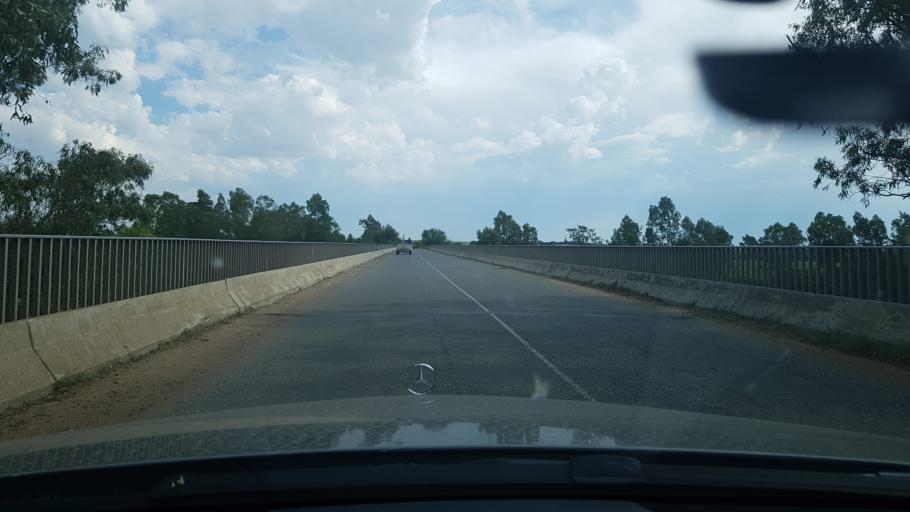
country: ZA
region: North-West
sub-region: Dr Ruth Segomotsi Mompati District Municipality
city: Bloemhof
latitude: -27.6539
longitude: 25.5956
